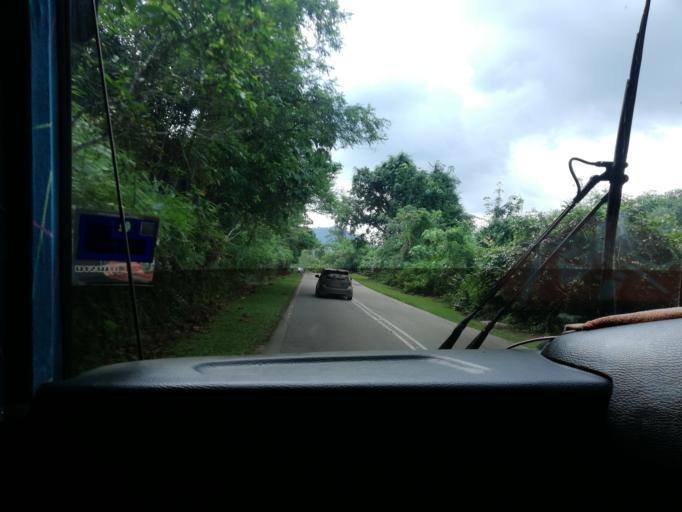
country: MY
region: Kedah
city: Kulim
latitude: 5.3192
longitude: 100.5985
